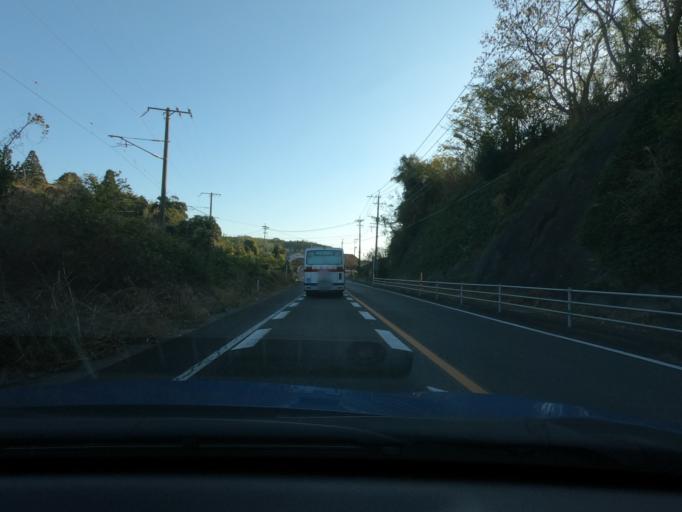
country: JP
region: Kagoshima
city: Akune
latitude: 31.9928
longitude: 130.1975
